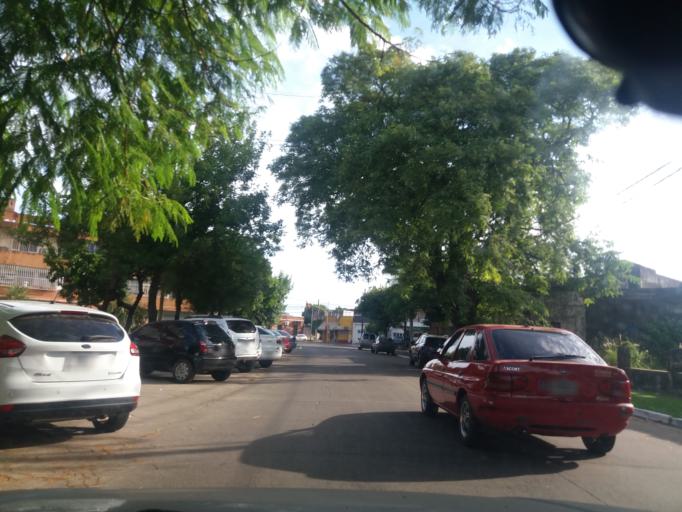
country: AR
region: Corrientes
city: Corrientes
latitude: -27.4839
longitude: -58.8318
